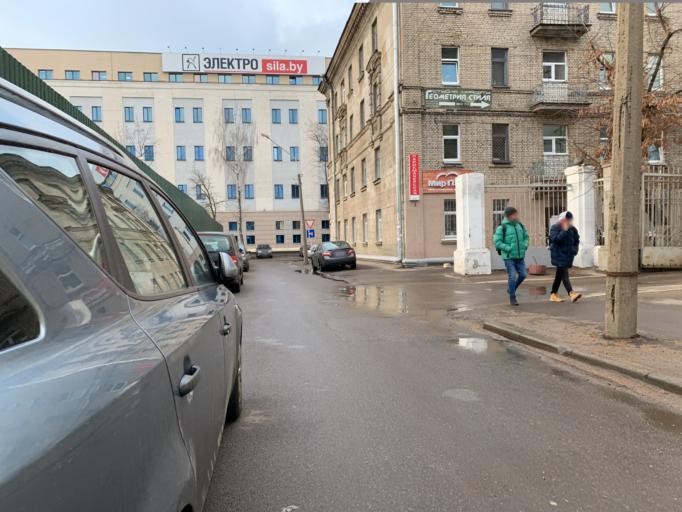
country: BY
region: Minsk
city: Minsk
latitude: 53.8892
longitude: 27.5377
